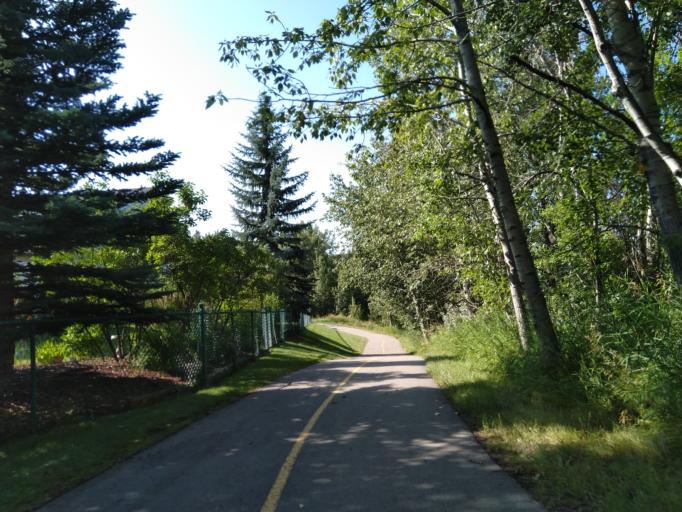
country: CA
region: Alberta
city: Calgary
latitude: 51.0960
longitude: -114.2480
